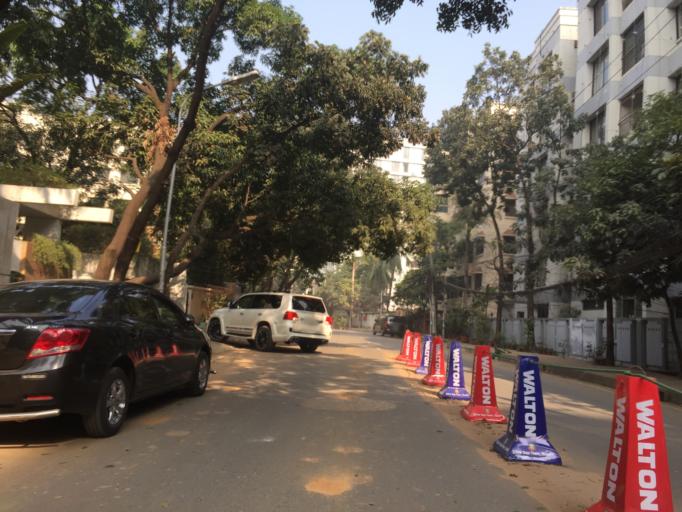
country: BD
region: Dhaka
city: Paltan
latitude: 23.7928
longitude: 90.4202
